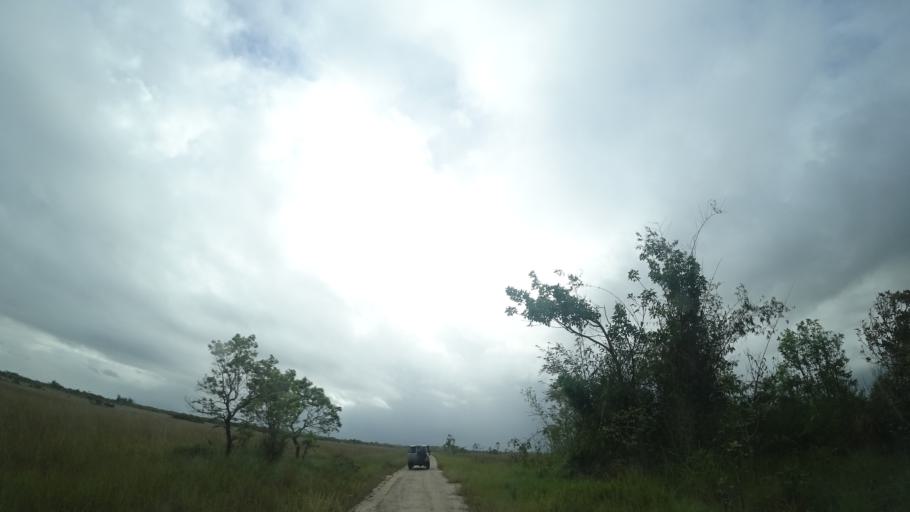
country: MZ
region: Sofala
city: Beira
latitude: -19.6160
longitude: 35.0628
